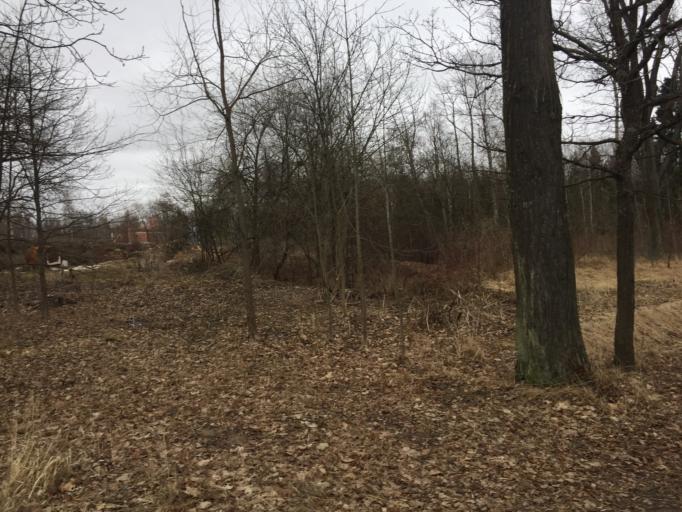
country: RU
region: St.-Petersburg
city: Pushkin
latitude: 59.7231
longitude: 30.3732
